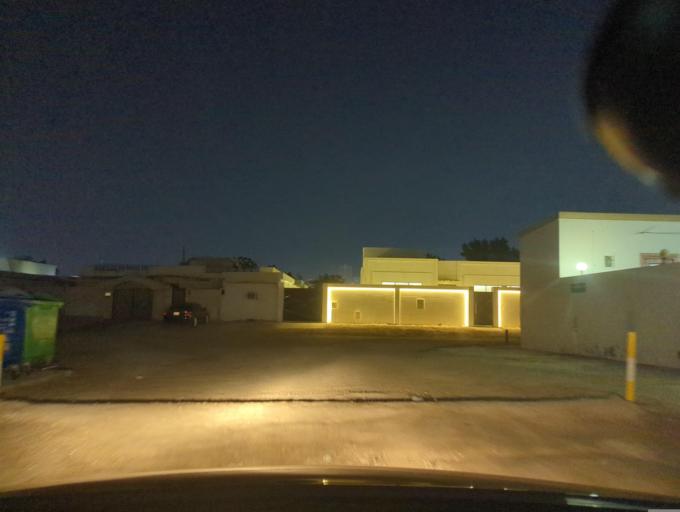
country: AE
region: Ajman
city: Ajman
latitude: 25.3806
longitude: 55.4450
